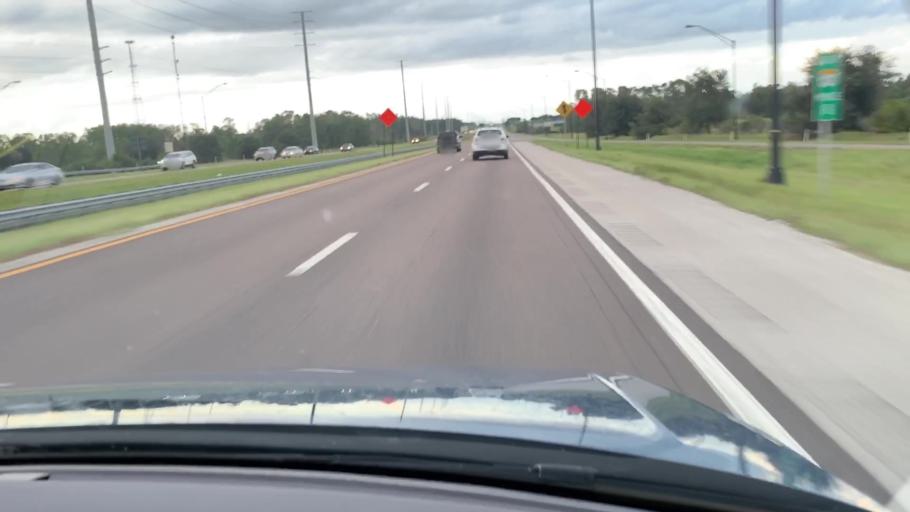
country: US
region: Florida
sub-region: Polk County
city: Citrus Ridge
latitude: 28.3815
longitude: -81.6129
